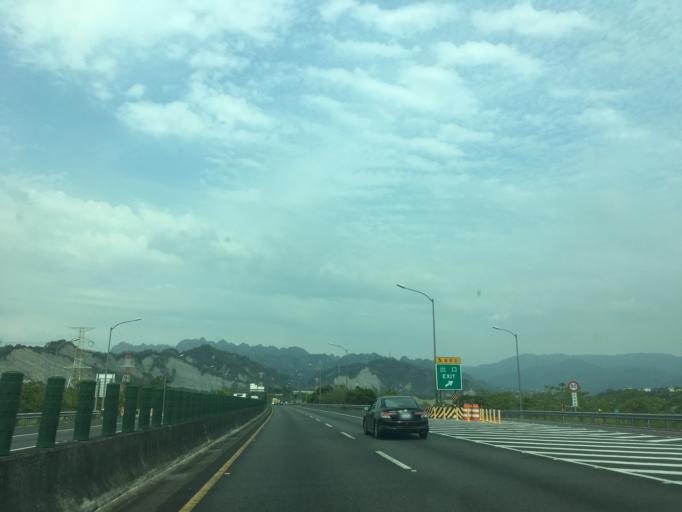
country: TW
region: Taiwan
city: Zhongxing New Village
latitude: 24.0069
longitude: 120.7163
